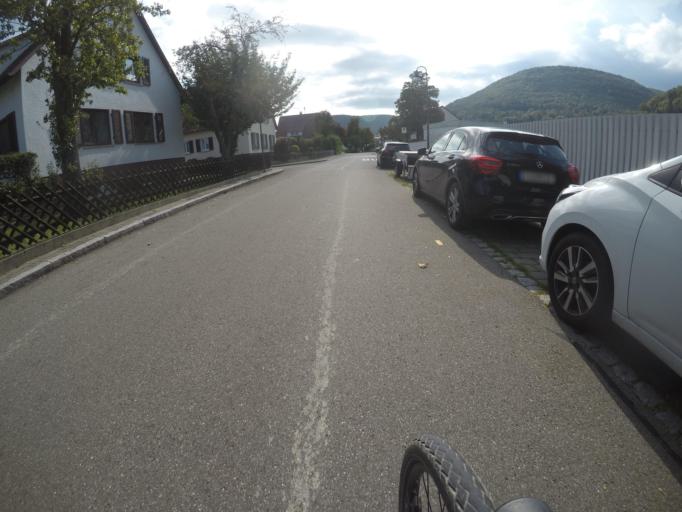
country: DE
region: Baden-Wuerttemberg
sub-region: Tuebingen Region
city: Bad Urach
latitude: 48.4980
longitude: 9.3842
